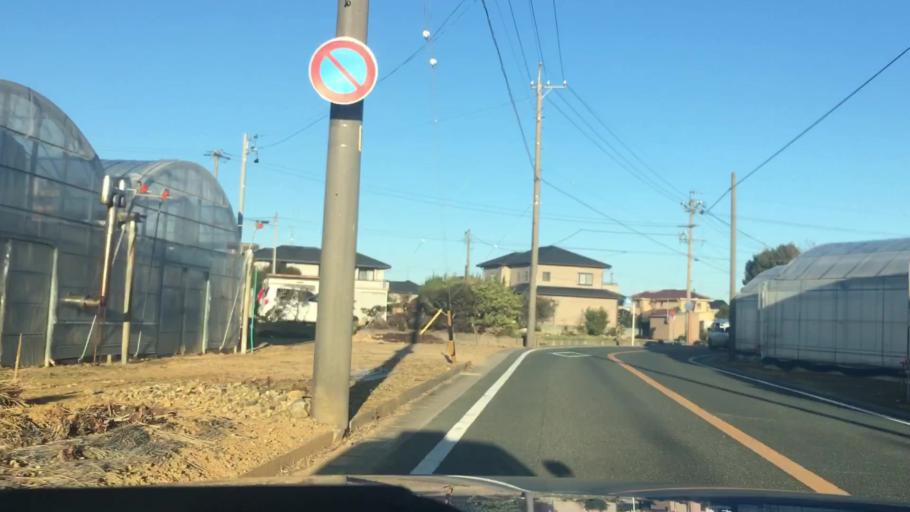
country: JP
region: Shizuoka
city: Hamamatsu
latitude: 34.7408
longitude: 137.6741
